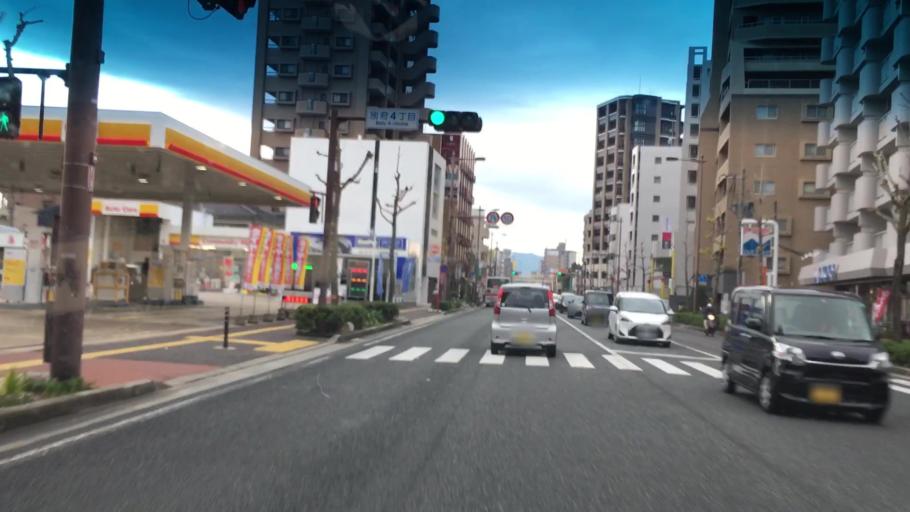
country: JP
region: Fukuoka
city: Fukuoka-shi
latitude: 33.5724
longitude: 130.3644
